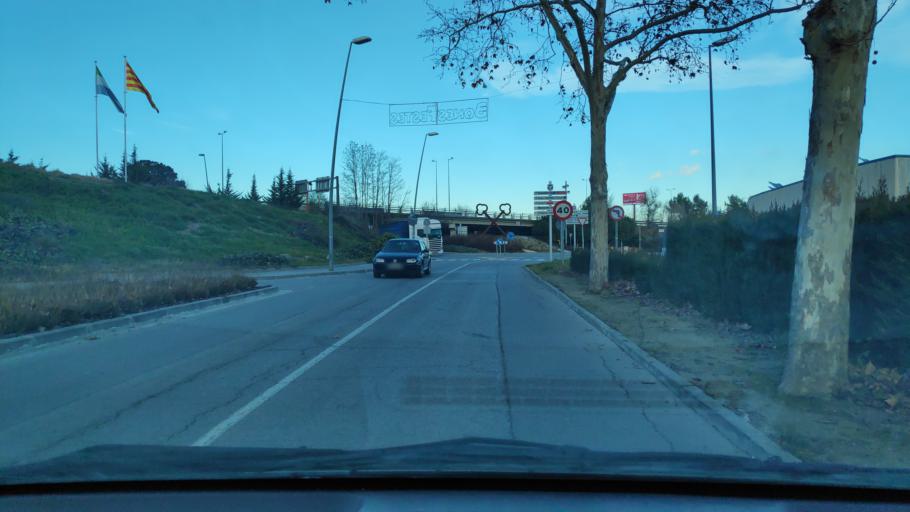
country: ES
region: Catalonia
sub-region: Provincia de Barcelona
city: Montmelo
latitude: 41.5578
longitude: 2.2531
